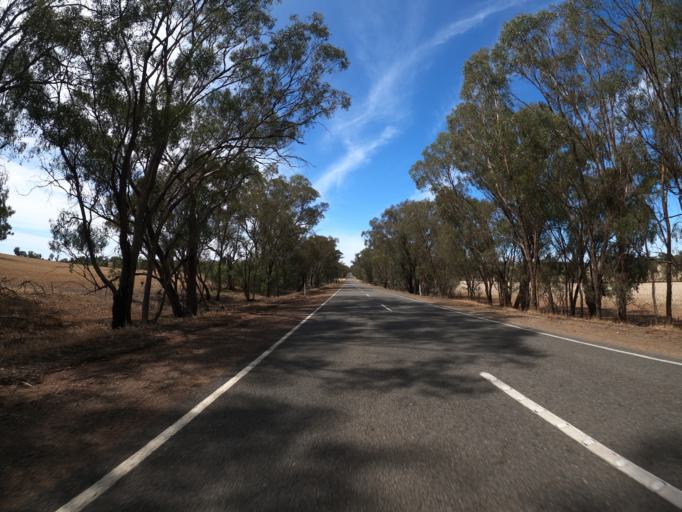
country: AU
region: Victoria
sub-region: Benalla
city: Benalla
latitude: -36.3520
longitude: 145.9634
